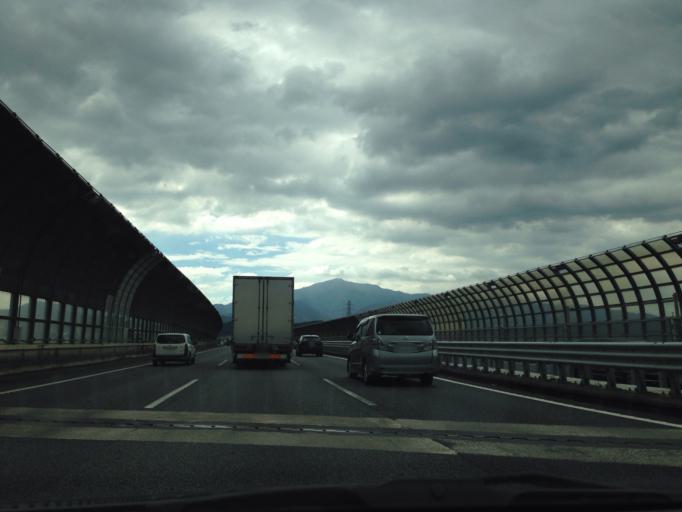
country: JP
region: Kanagawa
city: Atsugi
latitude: 35.4250
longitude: 139.3527
